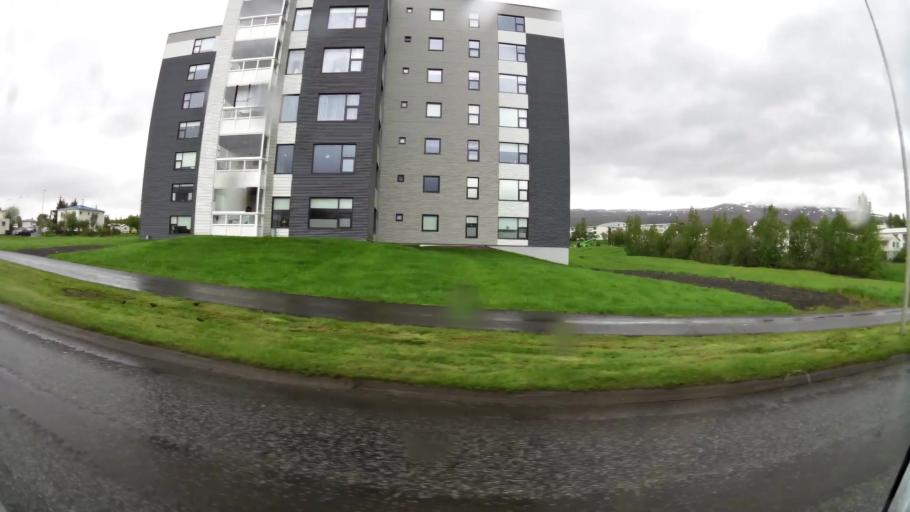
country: IS
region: Northeast
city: Akureyri
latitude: 65.6935
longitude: -18.1064
